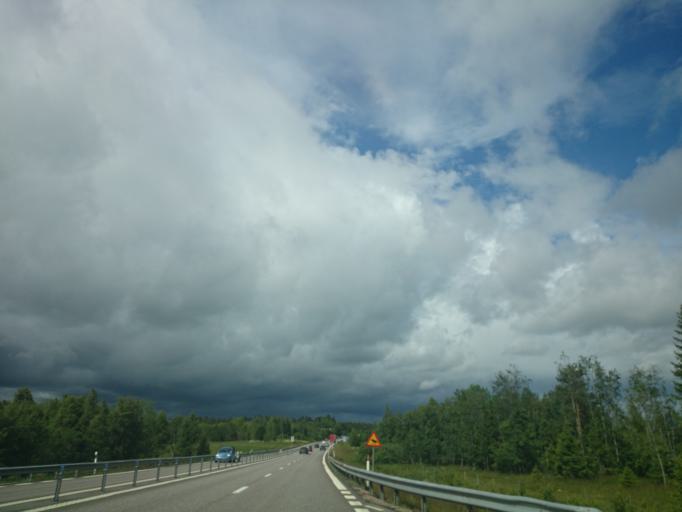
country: SE
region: Vaesternorrland
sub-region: Sundsvalls Kommun
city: Njurundabommen
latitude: 62.2229
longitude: 17.3718
